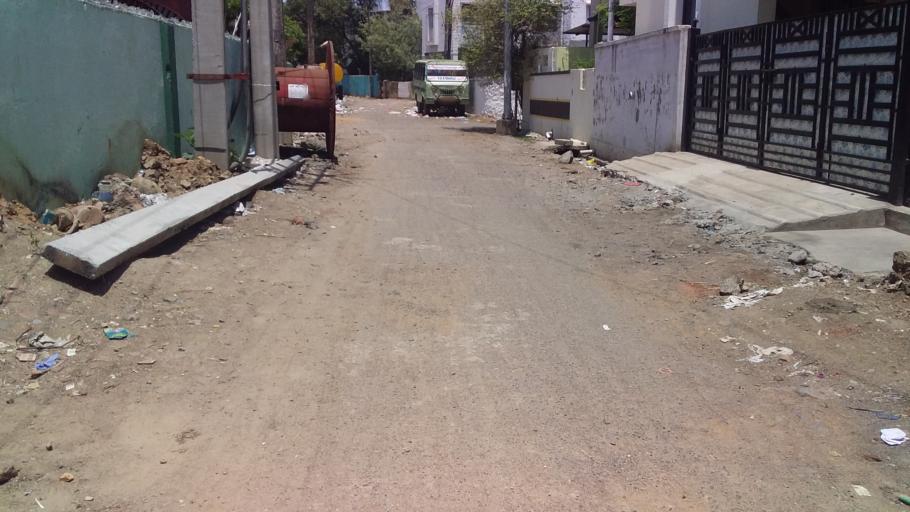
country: IN
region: Tamil Nadu
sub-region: Kancheepuram
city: Pallavaram
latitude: 12.9752
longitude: 80.1317
